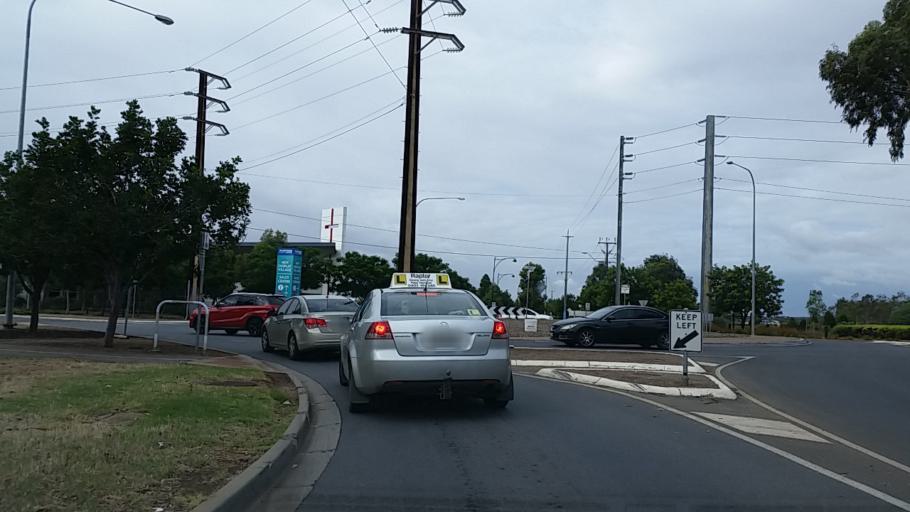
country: AU
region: South Australia
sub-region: Playford
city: Smithfield
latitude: -34.6747
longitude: 138.6845
